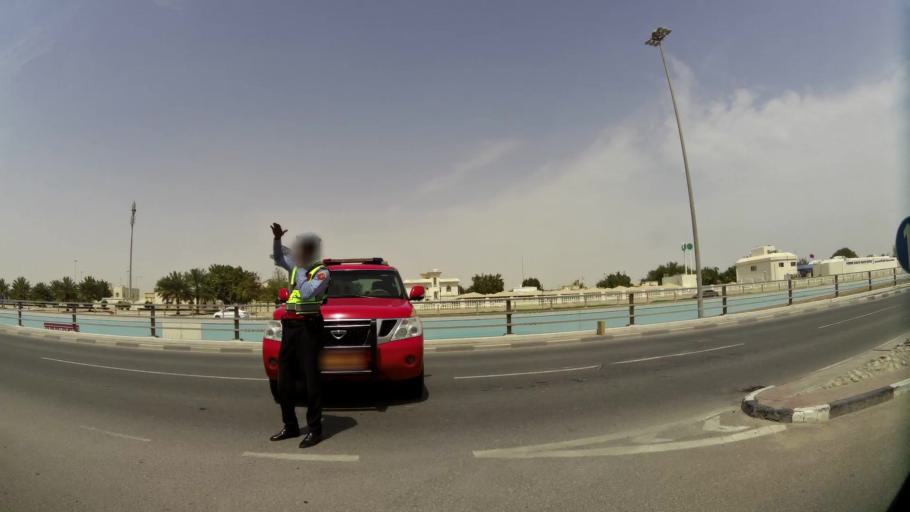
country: QA
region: Baladiyat ar Rayyan
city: Ar Rayyan
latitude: 25.3209
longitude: 51.4723
